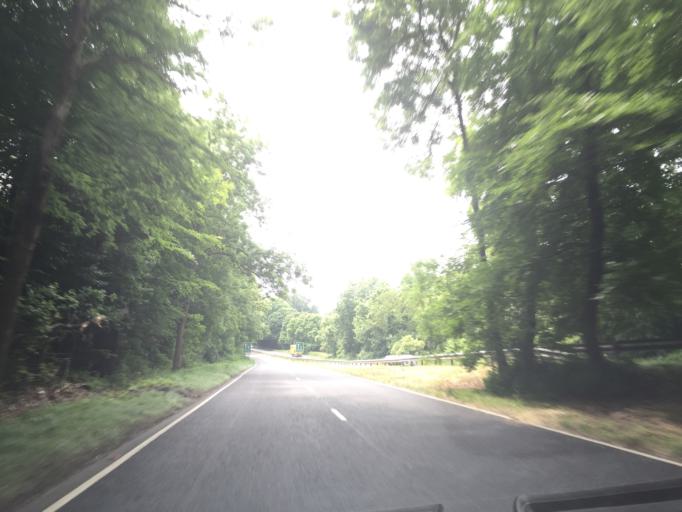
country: GB
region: England
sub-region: Hampshire
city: Long Sutton
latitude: 51.1802
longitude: -0.9115
